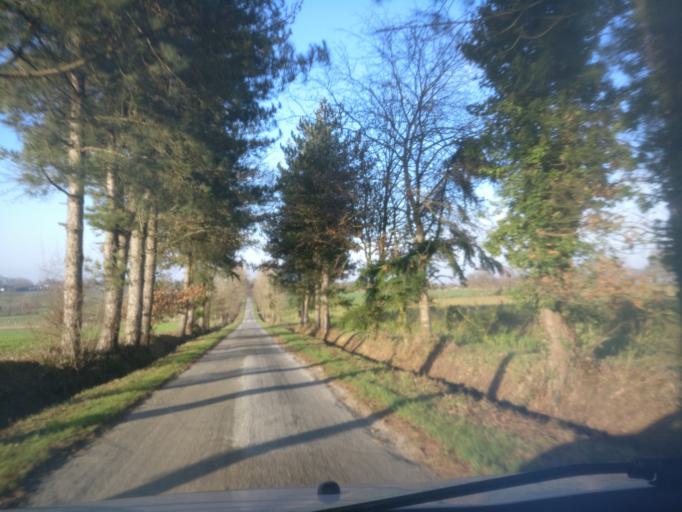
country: FR
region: Brittany
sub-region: Departement d'Ille-et-Vilaine
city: Livre-sur-Changeon
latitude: 48.1931
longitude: -1.3175
